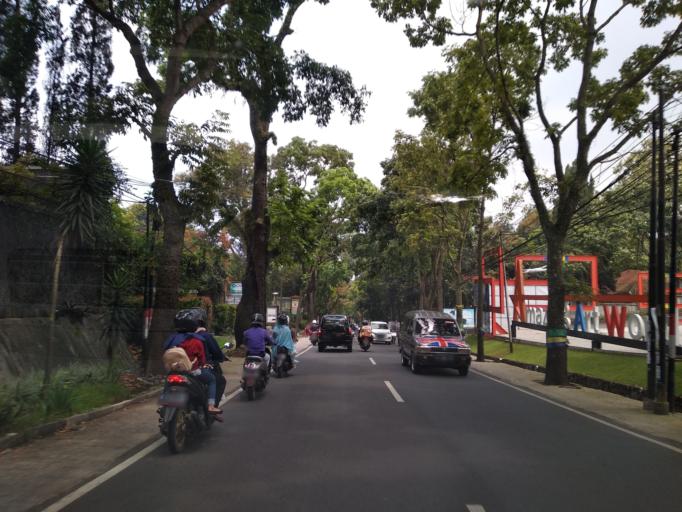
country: ID
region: West Java
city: Lembang
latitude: -6.8515
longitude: 107.5967
